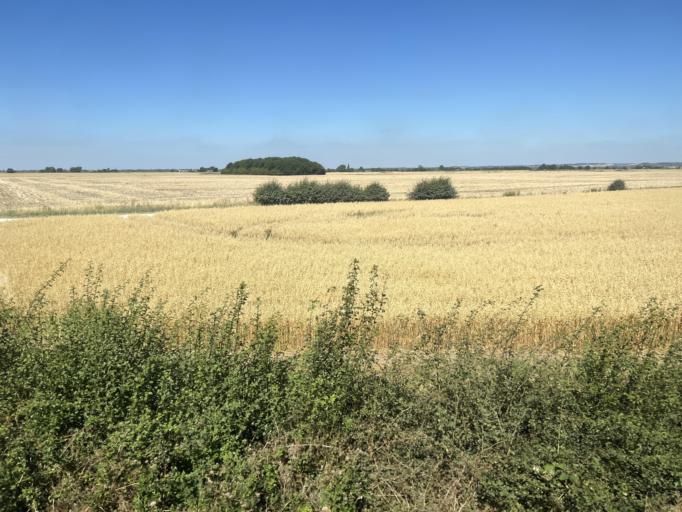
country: GB
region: England
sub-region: Lincolnshire
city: Spilsby
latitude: 53.0770
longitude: 0.0804
